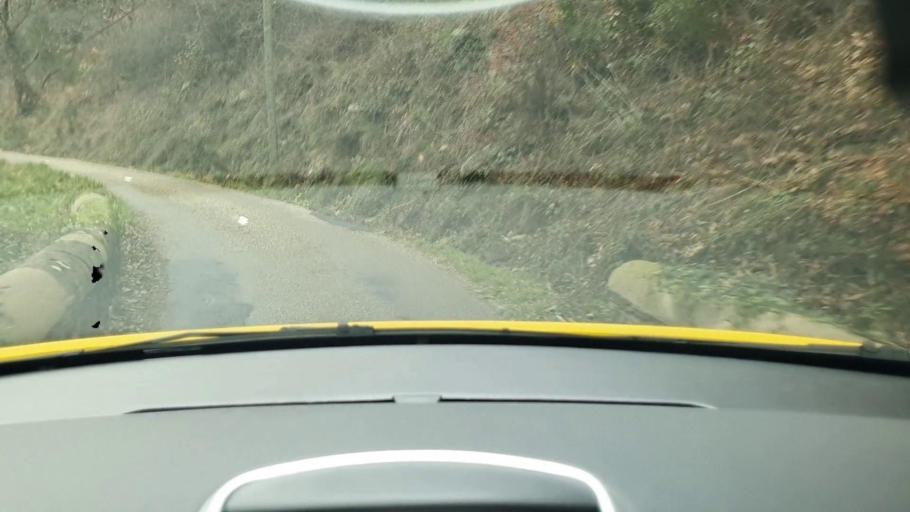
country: FR
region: Languedoc-Roussillon
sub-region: Departement du Gard
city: Besseges
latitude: 44.3736
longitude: 4.0400
